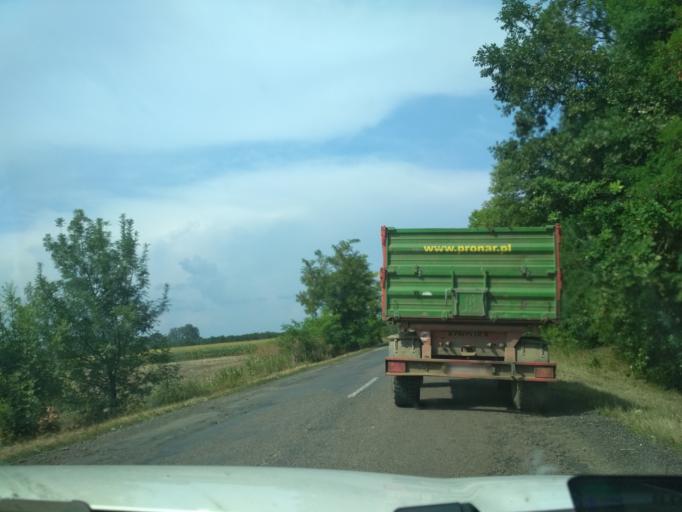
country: HU
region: Jasz-Nagykun-Szolnok
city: Abadszalok
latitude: 47.5003
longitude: 20.6276
